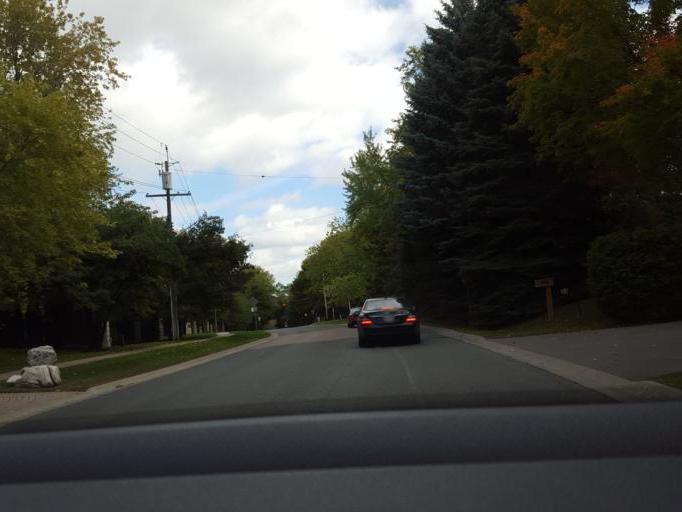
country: CA
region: Ontario
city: Willowdale
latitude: 43.7378
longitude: -79.3743
